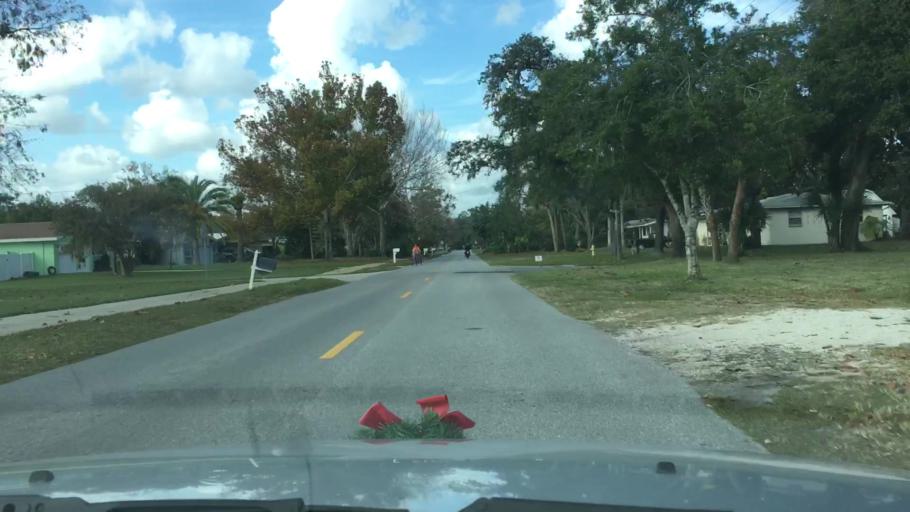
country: US
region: Florida
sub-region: Volusia County
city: Ormond Beach
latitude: 29.2950
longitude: -81.0685
